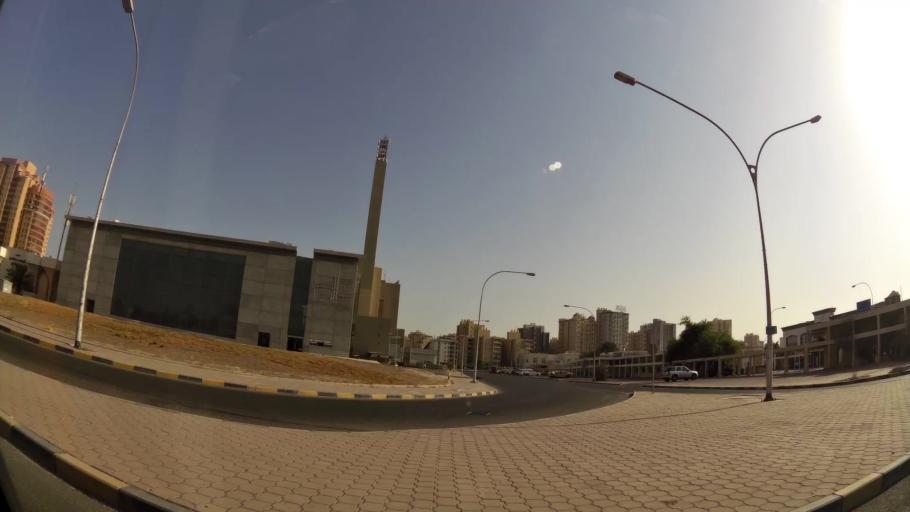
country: KW
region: Muhafazat Hawalli
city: As Salimiyah
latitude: 29.3401
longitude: 48.0818
